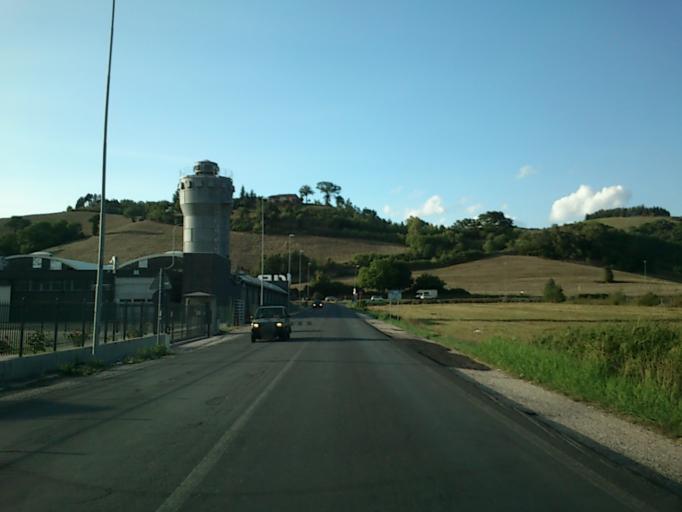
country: IT
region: The Marches
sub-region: Provincia di Pesaro e Urbino
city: Fermignano
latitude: 43.6975
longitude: 12.6624
